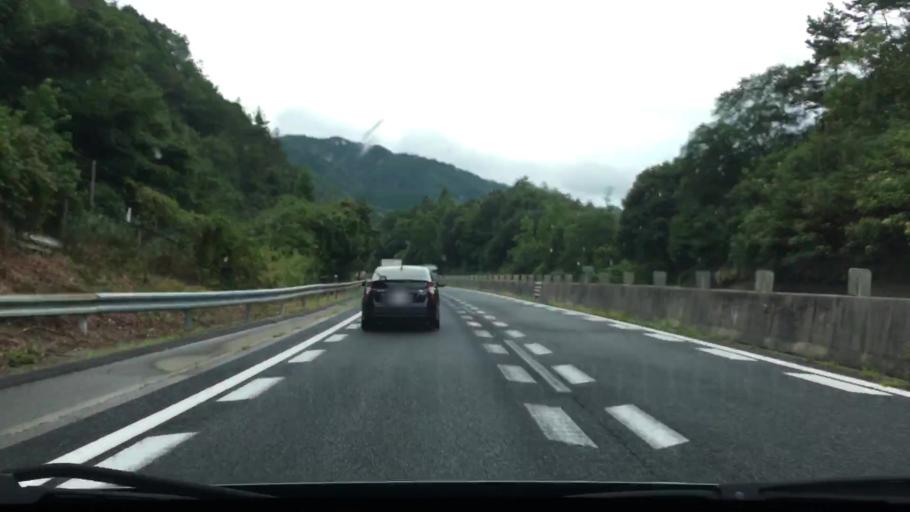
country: JP
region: Hiroshima
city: Hiroshima-shi
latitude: 34.5947
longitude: 132.4870
